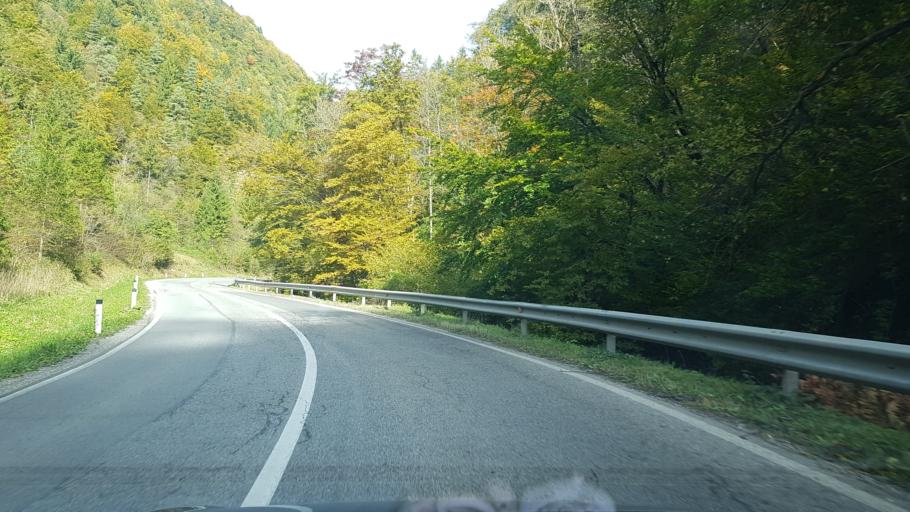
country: SI
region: Velenje
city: Velenje
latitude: 46.3900
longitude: 15.1655
